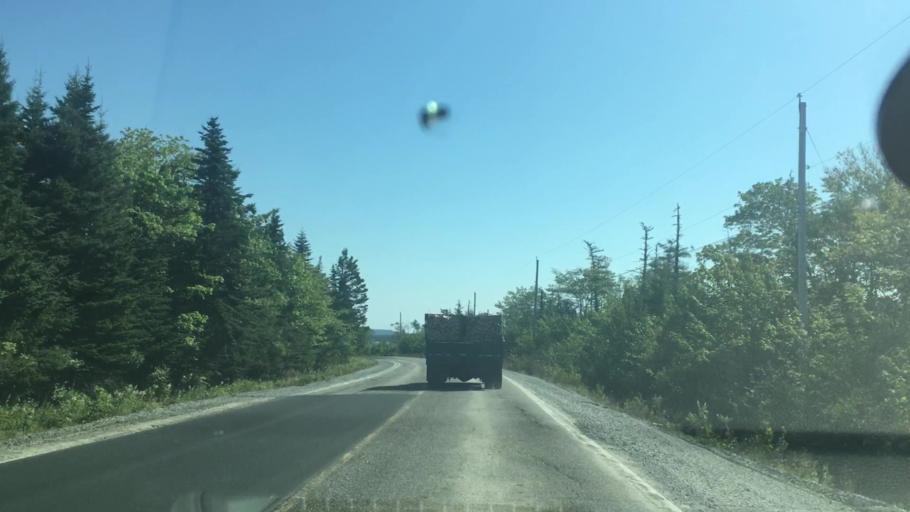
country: CA
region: Nova Scotia
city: New Glasgow
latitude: 44.8984
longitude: -62.4324
